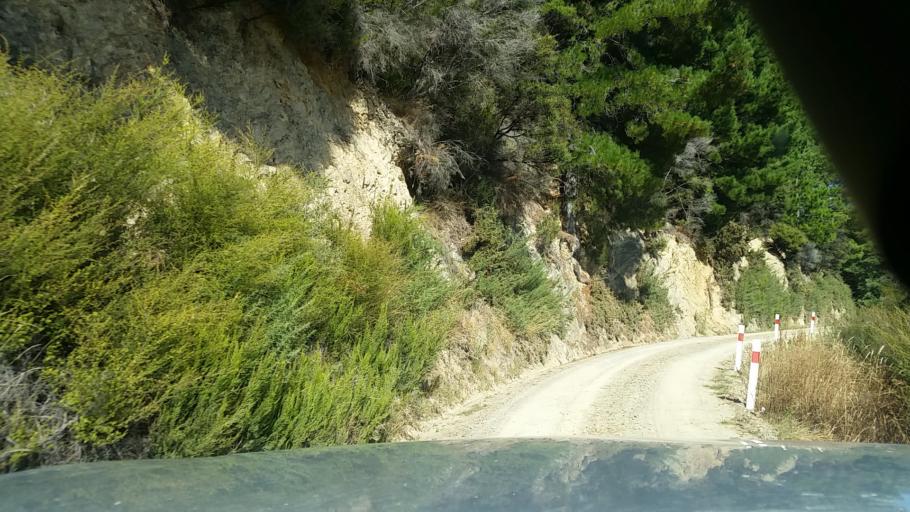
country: NZ
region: Marlborough
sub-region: Marlborough District
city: Picton
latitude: -41.3064
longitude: 174.1747
